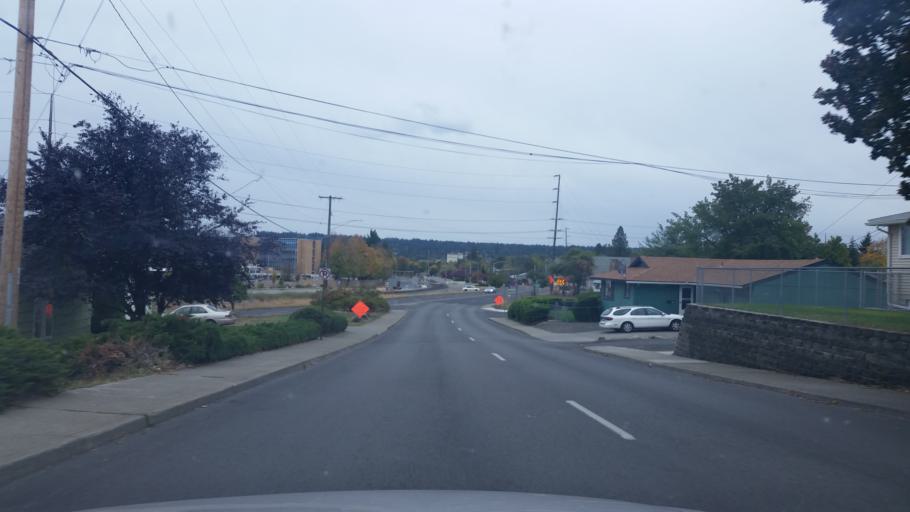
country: US
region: Washington
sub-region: Spokane County
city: Spokane
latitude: 47.6775
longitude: -117.3899
